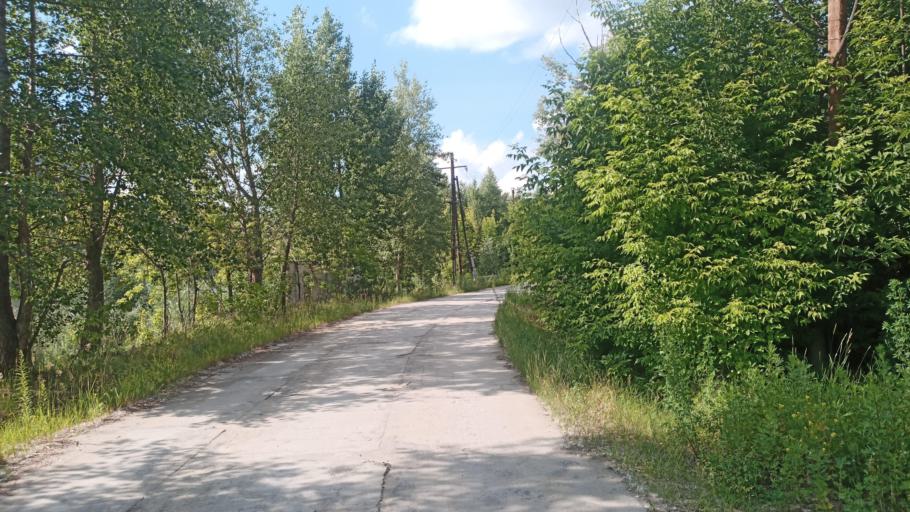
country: RU
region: Altai Krai
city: Zaton
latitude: 53.3396
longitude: 83.8060
